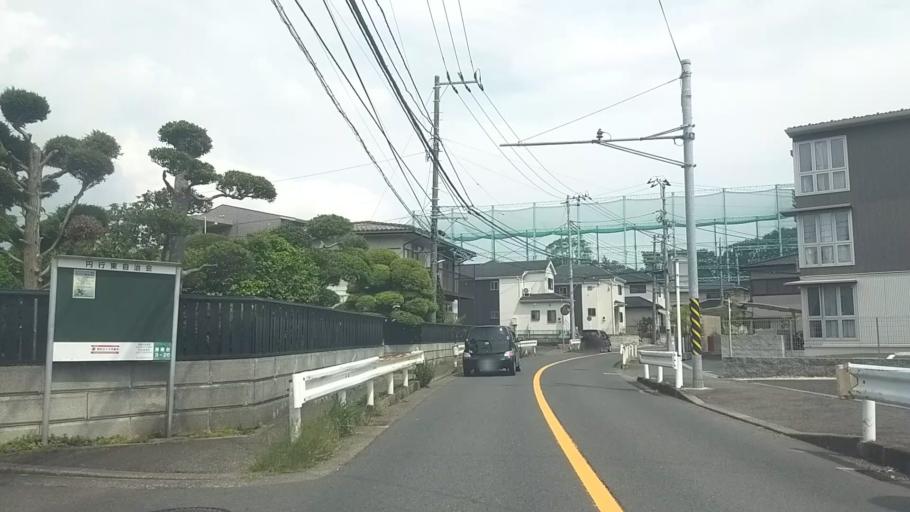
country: JP
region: Kanagawa
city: Fujisawa
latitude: 35.3897
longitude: 139.4619
